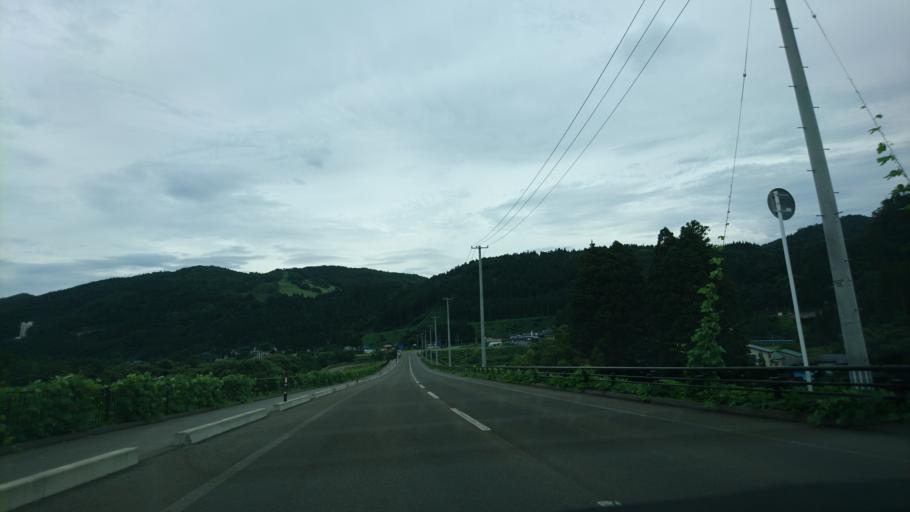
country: JP
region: Miyagi
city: Furukawa
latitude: 38.7394
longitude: 140.6998
